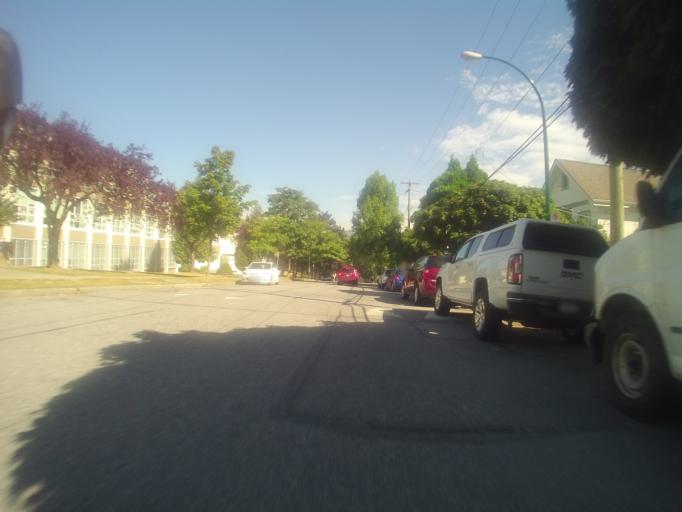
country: CA
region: British Columbia
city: Vancouver
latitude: 49.2483
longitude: -123.0605
